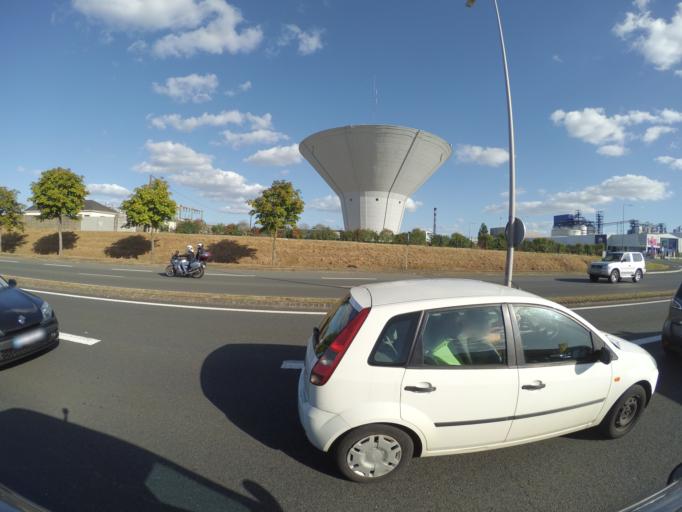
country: FR
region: Pays de la Loire
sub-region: Departement de Maine-et-Loire
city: Mazieres-en-Mauges
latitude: 47.0674
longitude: -0.8425
